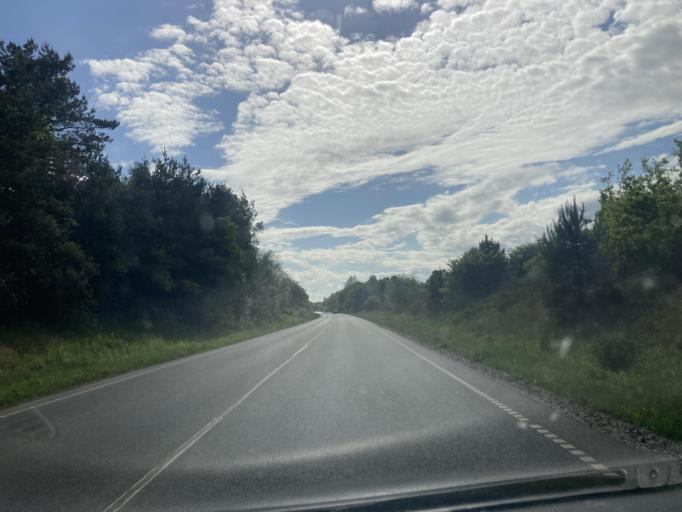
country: DK
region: Capital Region
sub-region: Gribskov Kommune
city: Helsinge
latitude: 56.0211
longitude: 12.1642
